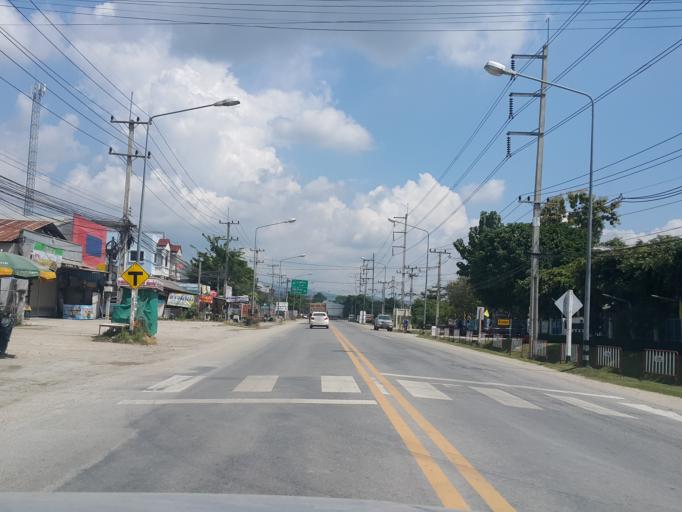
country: TH
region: Chiang Mai
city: San Sai
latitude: 18.9204
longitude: 98.9917
